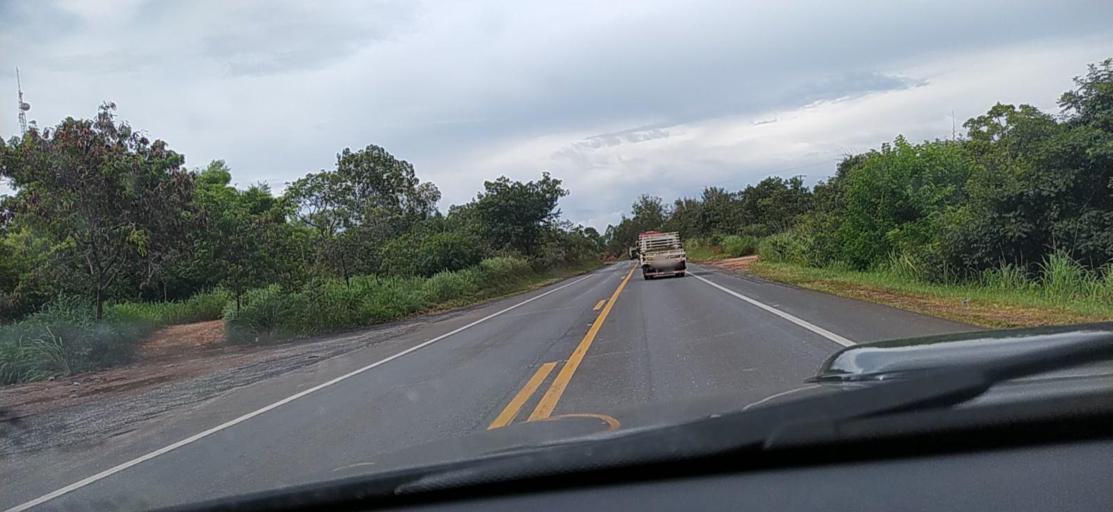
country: BR
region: Minas Gerais
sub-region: Montes Claros
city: Montes Claros
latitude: -16.8410
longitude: -43.8496
